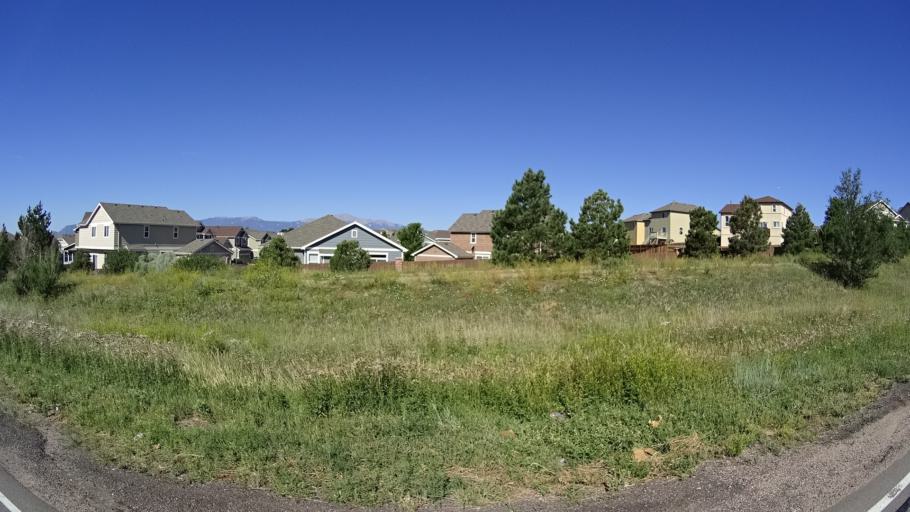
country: US
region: Colorado
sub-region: El Paso County
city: Cimarron Hills
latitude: 38.9061
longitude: -104.6829
